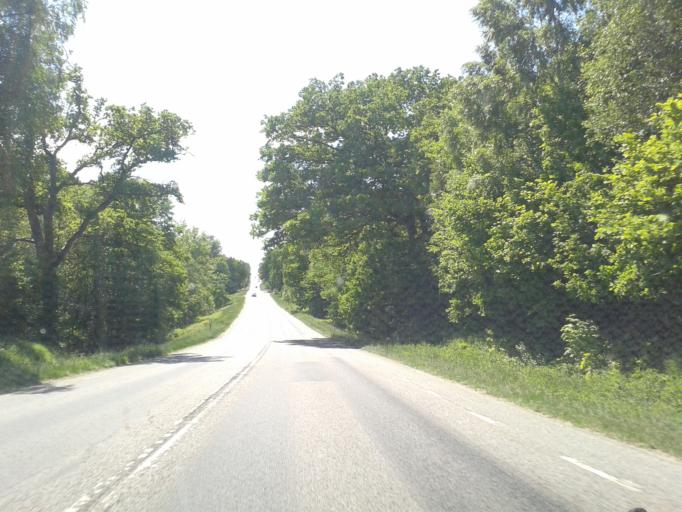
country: SE
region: Vaestra Goetaland
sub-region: Stenungsunds Kommun
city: Stora Hoga
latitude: 58.0659
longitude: 11.9265
